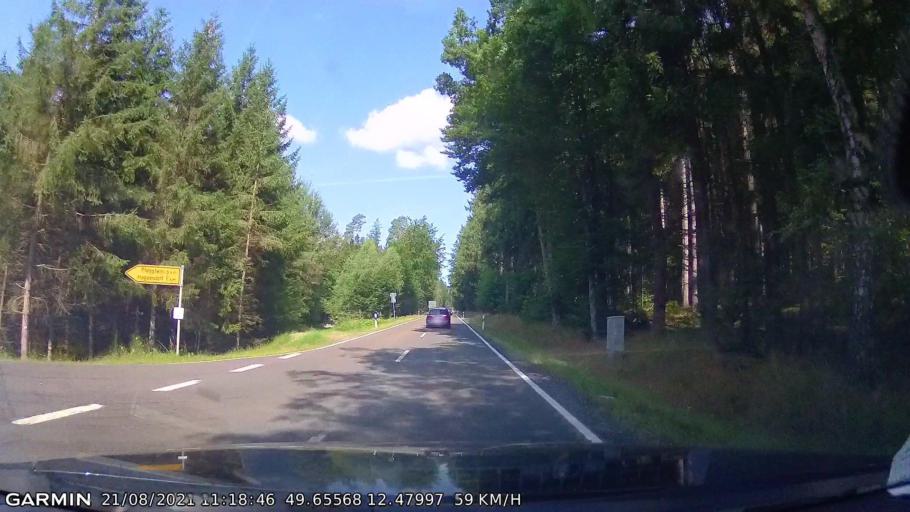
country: DE
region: Bavaria
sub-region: Upper Palatinate
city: Waidhaus
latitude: 49.6558
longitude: 12.4798
